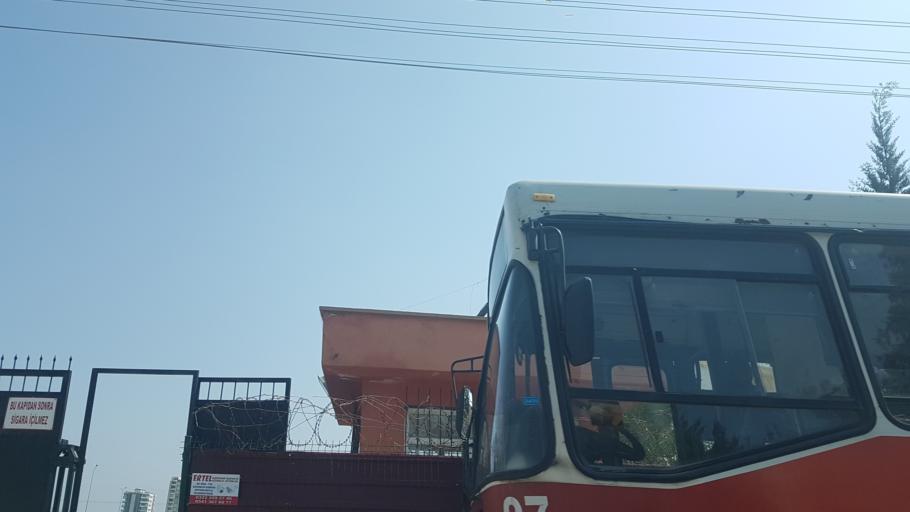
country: TR
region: Adana
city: Adana
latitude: 37.0089
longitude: 35.3512
